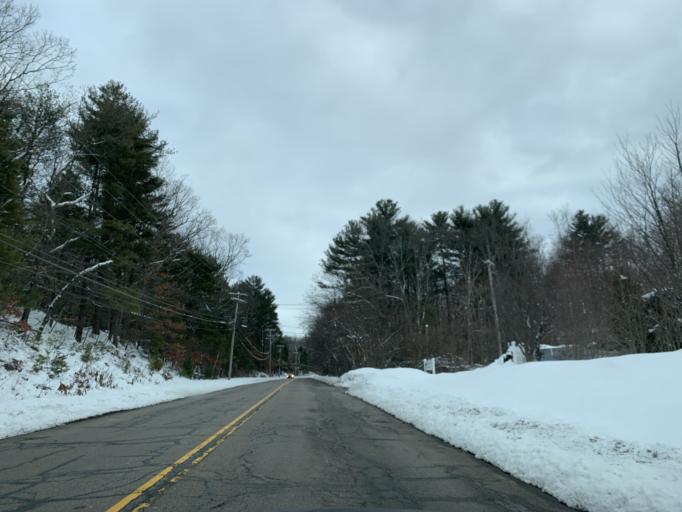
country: US
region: Massachusetts
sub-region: Norfolk County
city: Franklin
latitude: 42.0853
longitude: -71.4263
